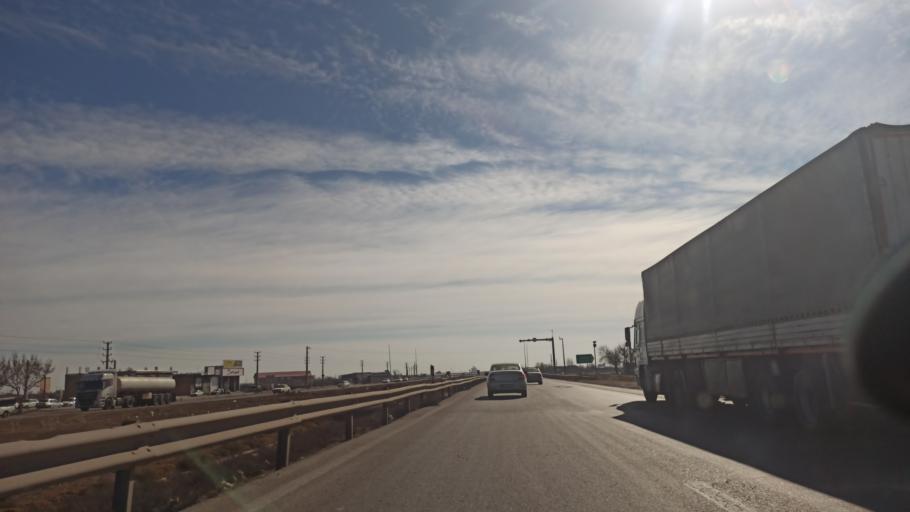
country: IR
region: Qazvin
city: Alvand
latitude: 36.1569
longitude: 50.0199
